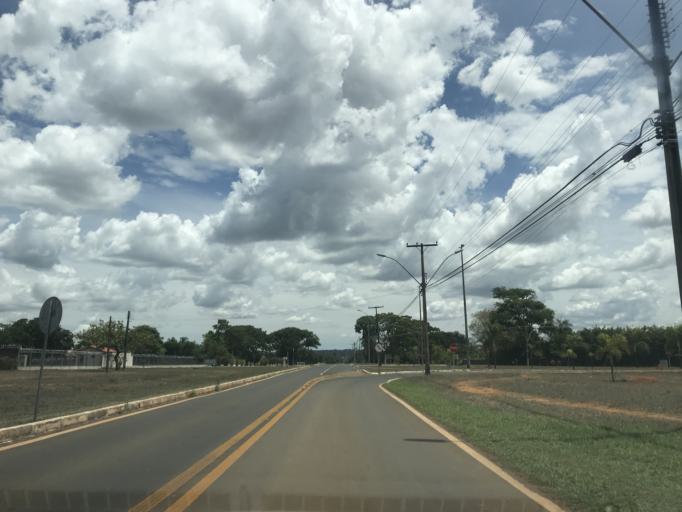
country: BR
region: Federal District
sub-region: Brasilia
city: Brasilia
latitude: -15.9085
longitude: -47.9462
